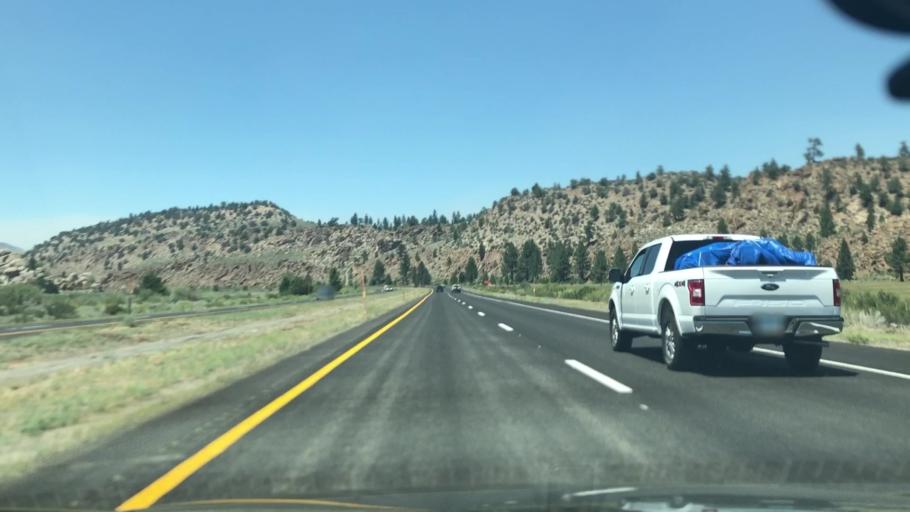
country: US
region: California
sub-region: Mono County
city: Mammoth Lakes
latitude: 37.5679
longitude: -118.6909
